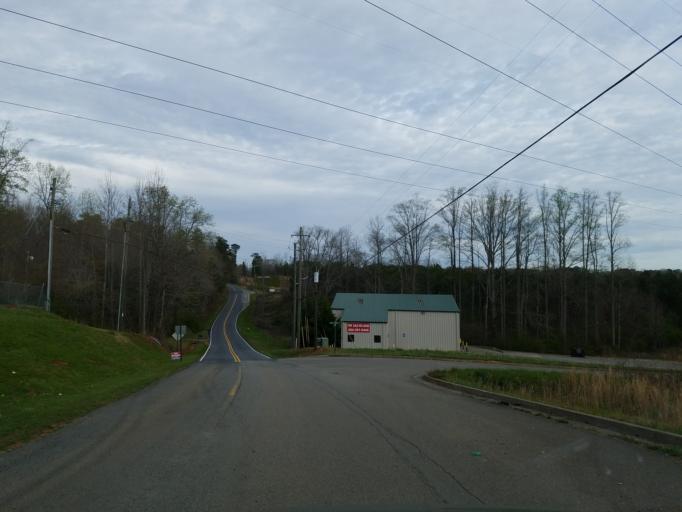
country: US
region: Georgia
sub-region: Pickens County
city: Jasper
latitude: 34.4746
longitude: -84.4570
